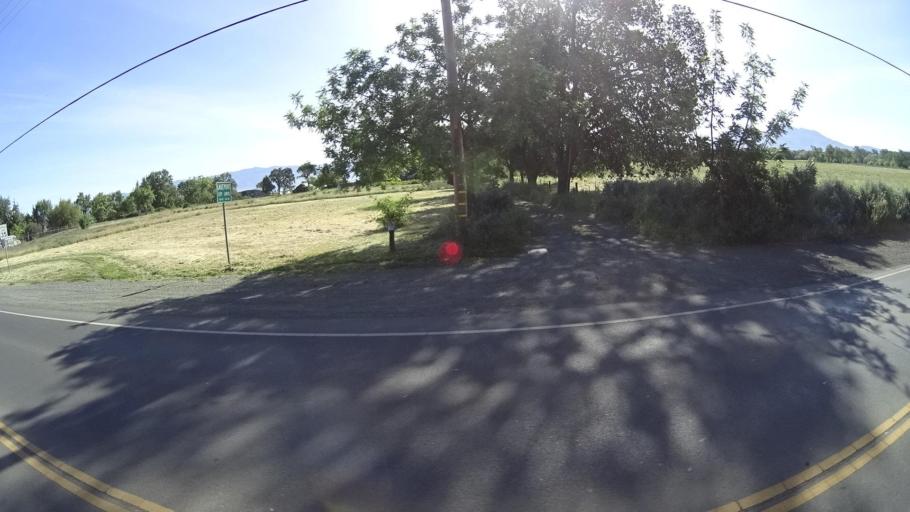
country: US
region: California
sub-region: Lake County
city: Lakeport
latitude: 39.0240
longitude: -122.9153
